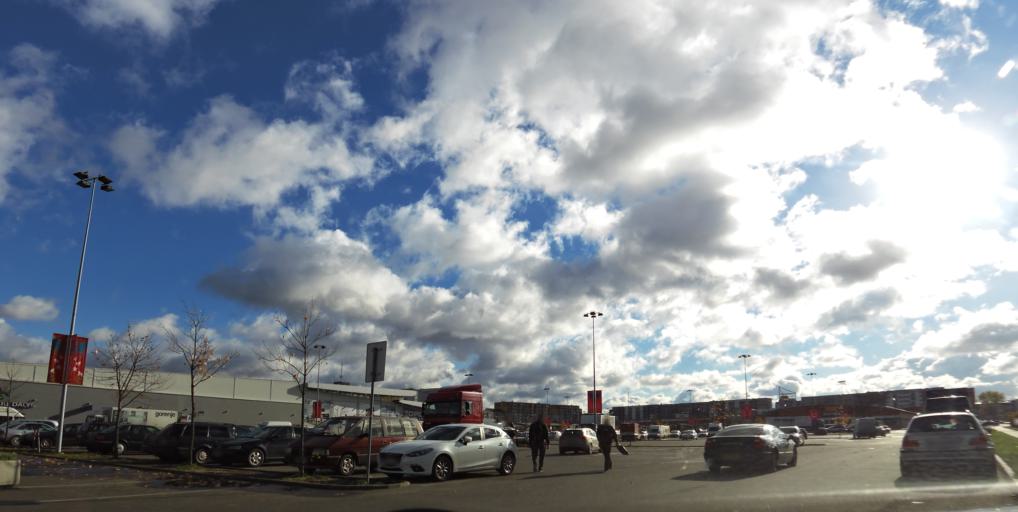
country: LT
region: Vilnius County
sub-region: Vilnius
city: Vilnius
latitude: 54.7129
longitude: 25.2995
